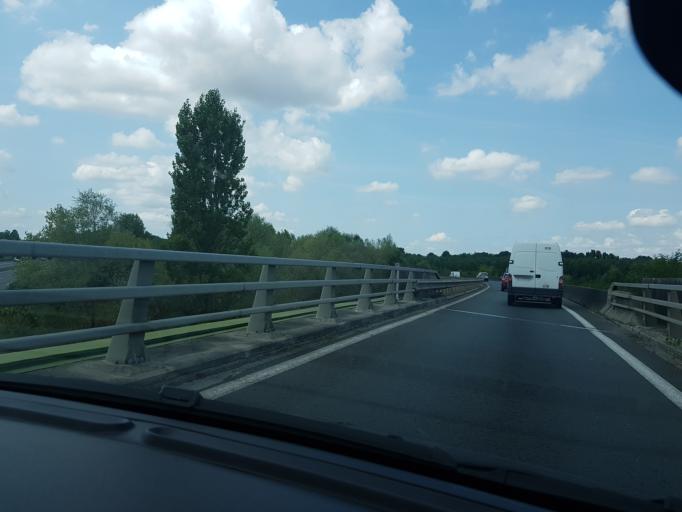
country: FR
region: Aquitaine
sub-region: Departement de la Gironde
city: Arveyres
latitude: 44.8722
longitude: -0.2806
